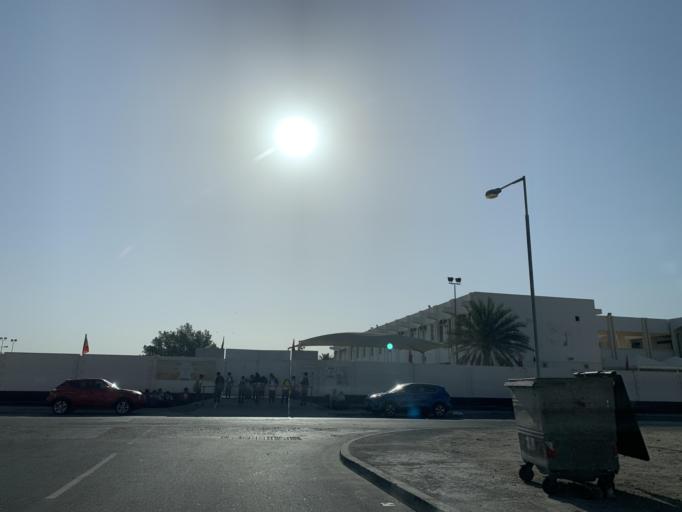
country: BH
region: Muharraq
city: Al Muharraq
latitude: 26.2631
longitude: 50.6048
